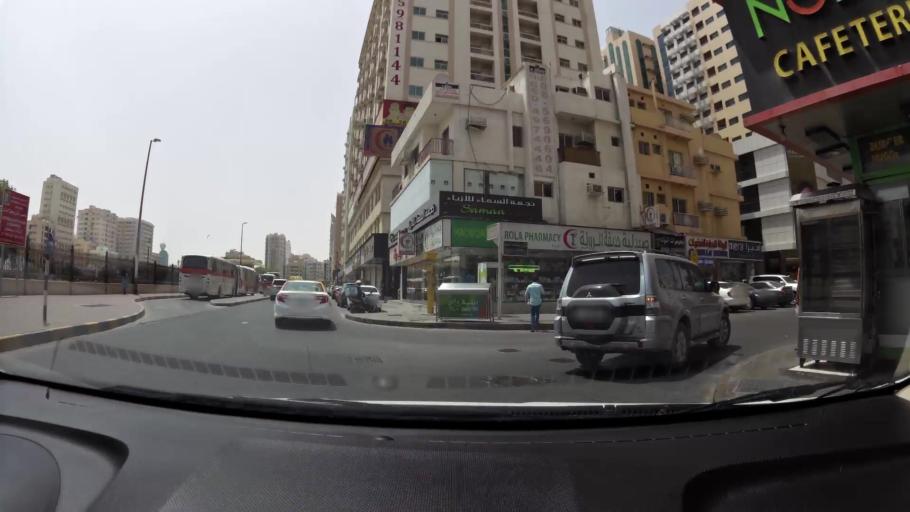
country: AE
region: Ash Shariqah
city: Sharjah
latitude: 25.3570
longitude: 55.3887
